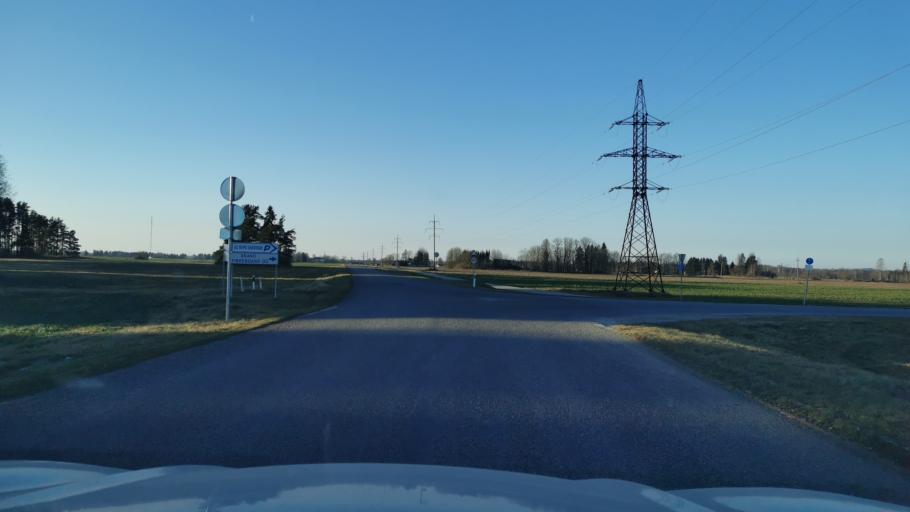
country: EE
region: Ida-Virumaa
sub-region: Puessi linn
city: Pussi
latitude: 59.3433
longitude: 27.0418
